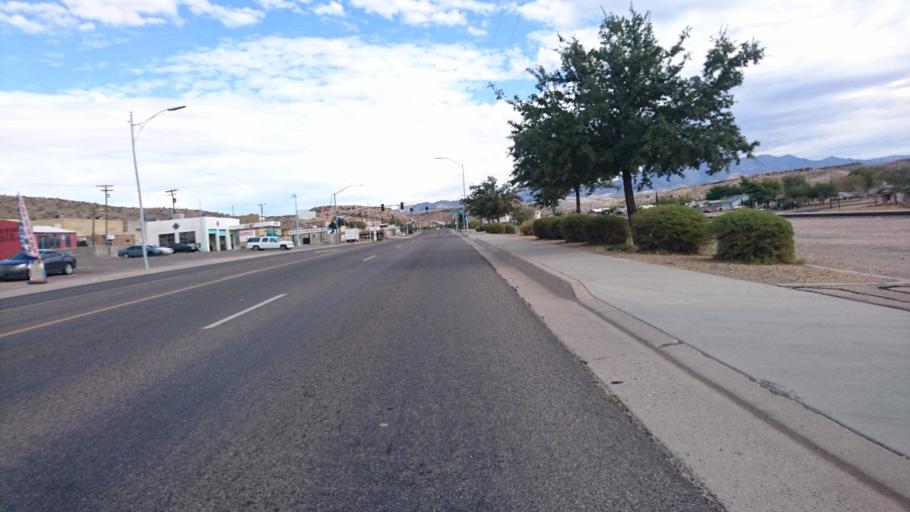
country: US
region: Arizona
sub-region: Mohave County
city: Kingman
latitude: 35.1875
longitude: -114.0472
